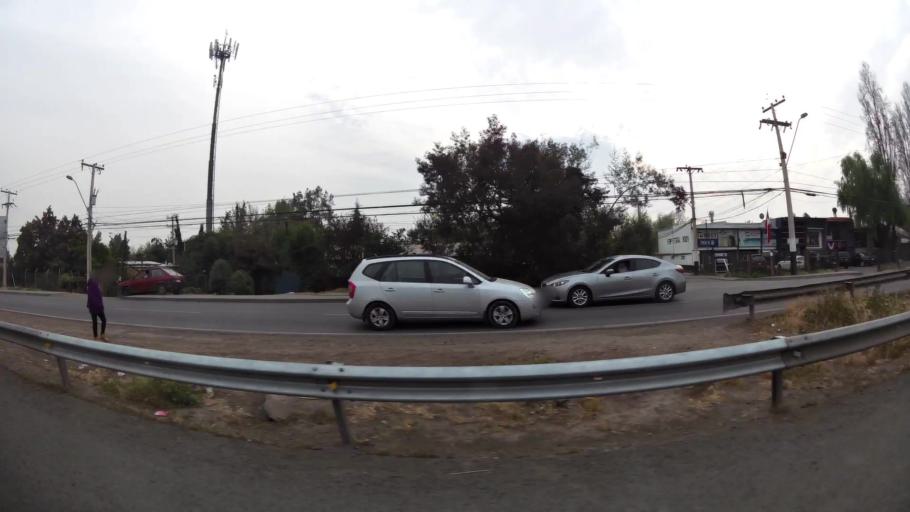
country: CL
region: Santiago Metropolitan
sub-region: Provincia de Chacabuco
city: Chicureo Abajo
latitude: -33.2460
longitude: -70.6979
